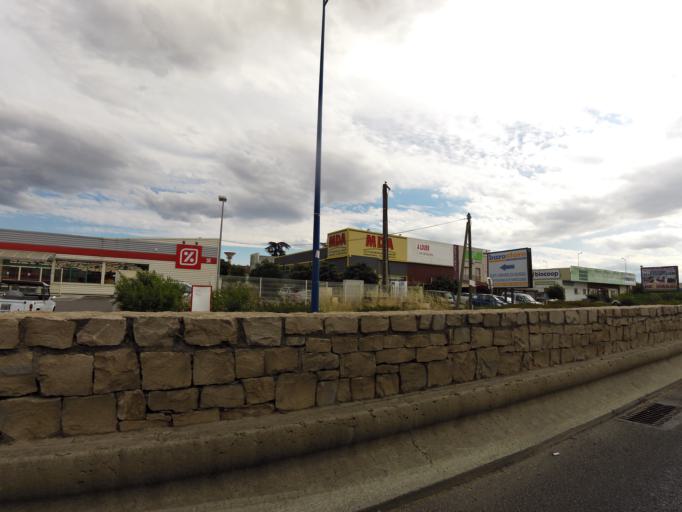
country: FR
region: Languedoc-Roussillon
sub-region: Departement de l'Herault
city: Le Cres
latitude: 43.6385
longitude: 3.9326
